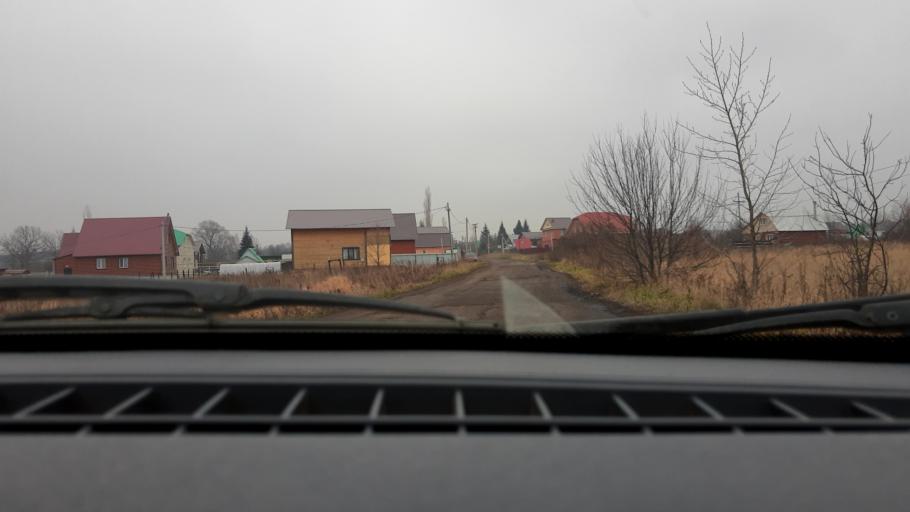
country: RU
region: Bashkortostan
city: Mikhaylovka
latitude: 54.8583
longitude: 55.8185
